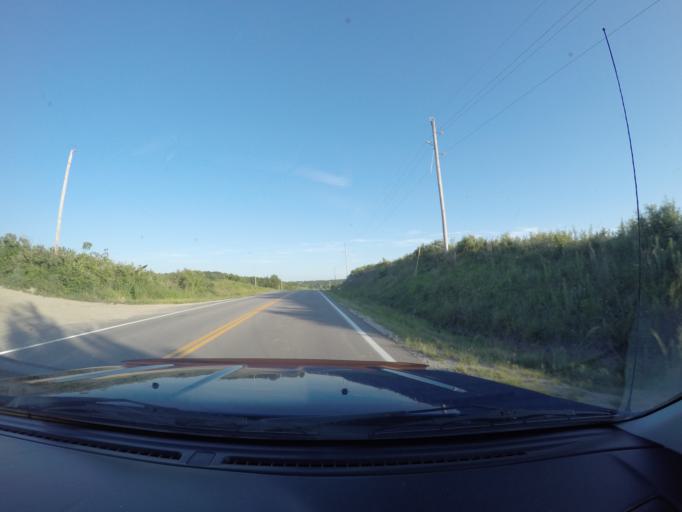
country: US
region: Kansas
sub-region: Pottawatomie County
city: Wamego
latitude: 39.1365
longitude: -96.3028
